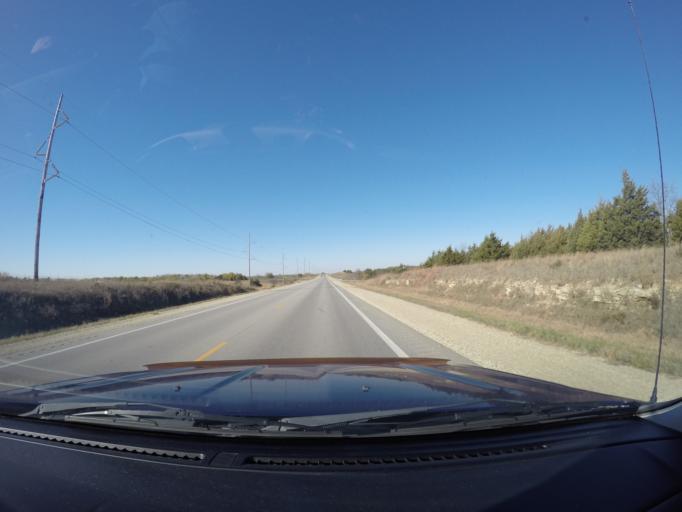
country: US
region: Kansas
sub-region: Riley County
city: Ogden
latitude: 39.2762
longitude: -96.7152
